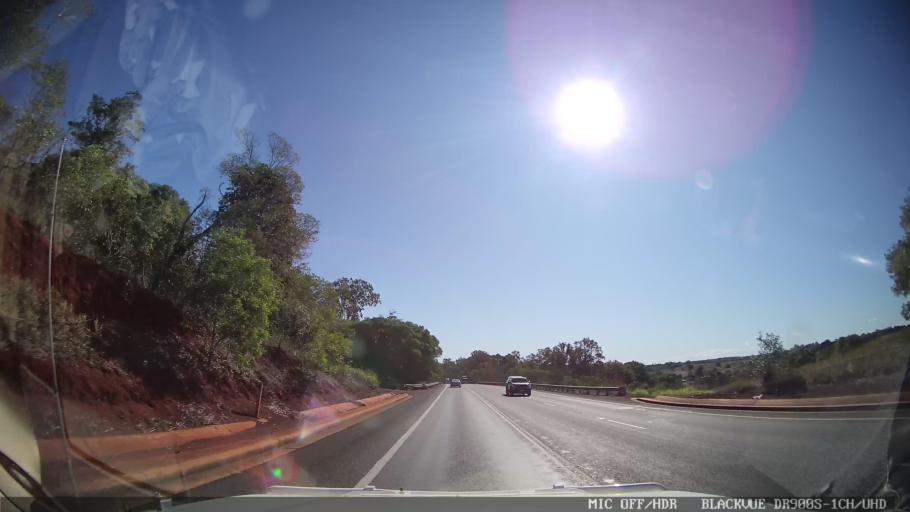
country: AU
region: Queensland
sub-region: Bundaberg
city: Childers
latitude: -25.2356
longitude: 152.2510
